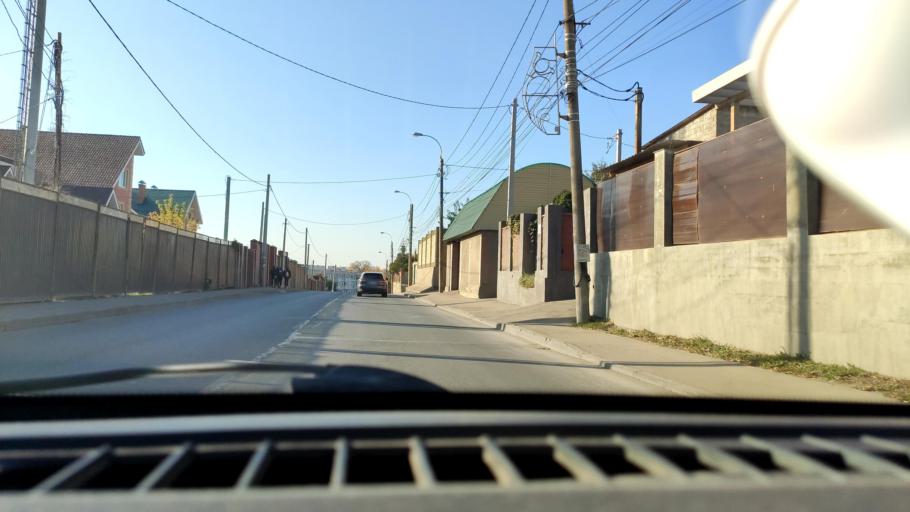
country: RU
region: Samara
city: Samara
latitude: 53.2671
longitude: 50.2024
